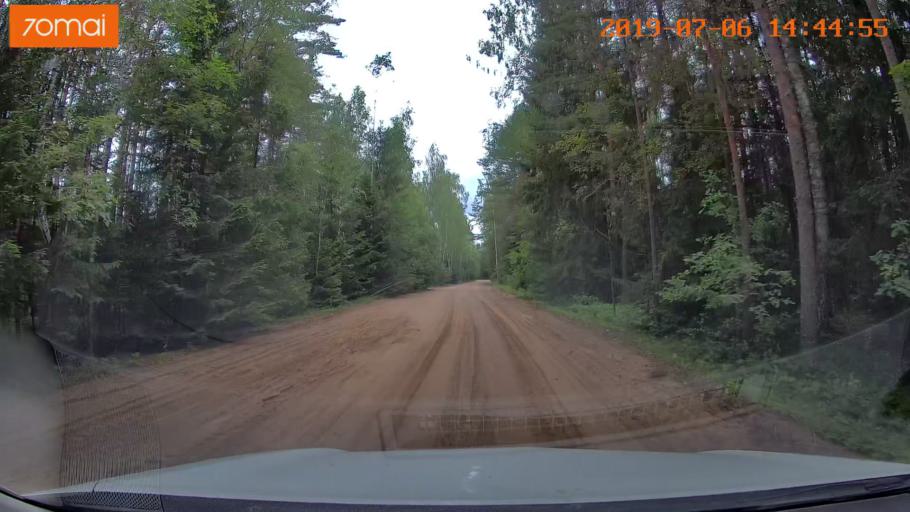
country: BY
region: Minsk
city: Ivyanyets
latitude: 53.9669
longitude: 26.6902
